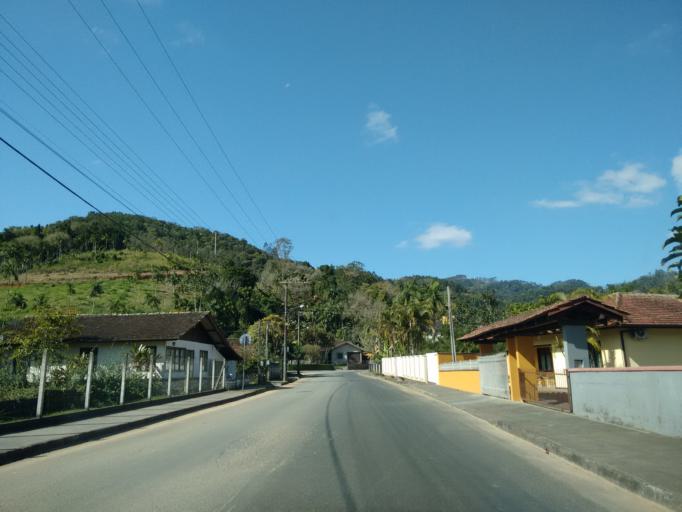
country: BR
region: Santa Catarina
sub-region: Pomerode
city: Pomerode
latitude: -26.7390
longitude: -49.1642
